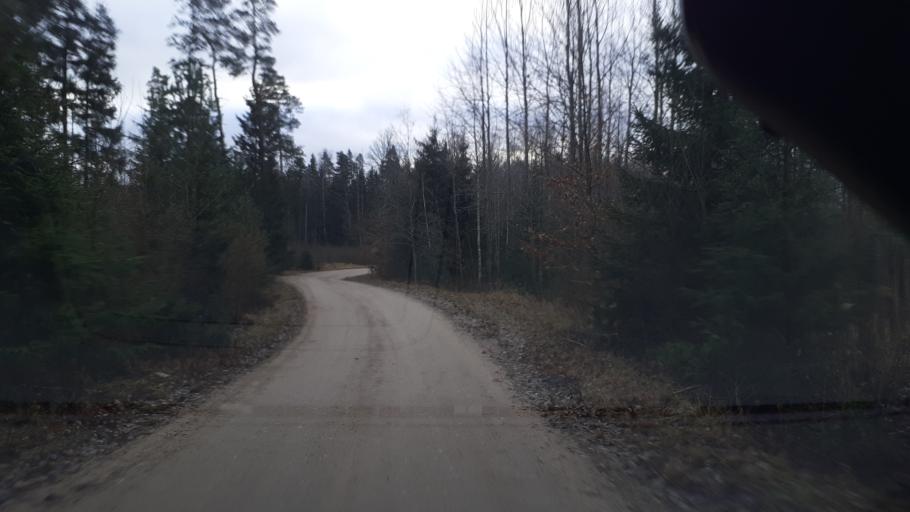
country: LV
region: Kuldigas Rajons
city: Kuldiga
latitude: 56.9031
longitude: 21.9084
